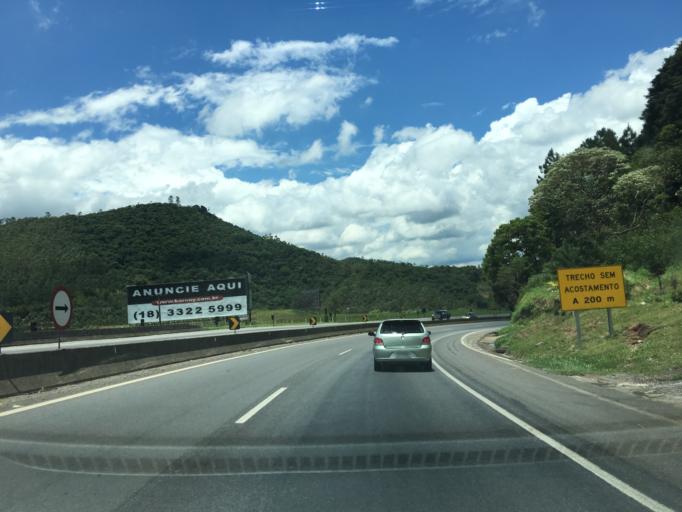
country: BR
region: Sao Paulo
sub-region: Mairipora
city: Mairipora
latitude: -23.2893
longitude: -46.5834
